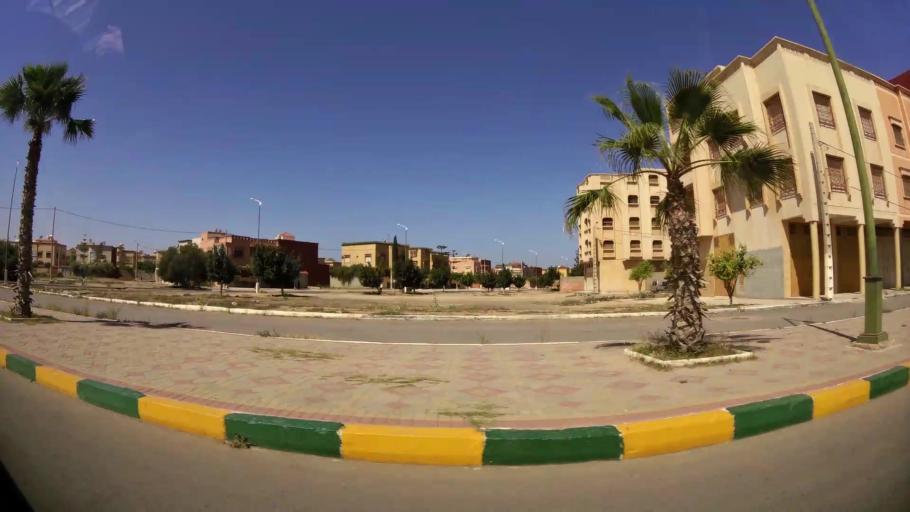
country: MA
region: Souss-Massa-Draa
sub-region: Inezgane-Ait Mellou
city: Inezgane
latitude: 30.3260
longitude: -9.5037
